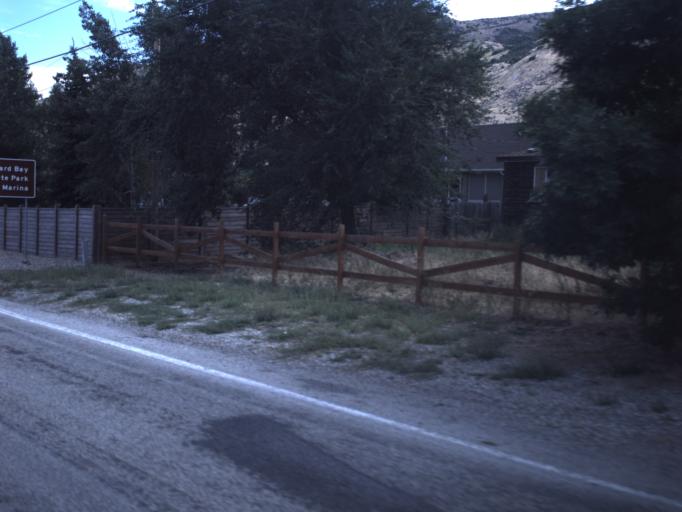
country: US
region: Utah
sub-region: Box Elder County
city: Willard
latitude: 41.4211
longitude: -112.0358
